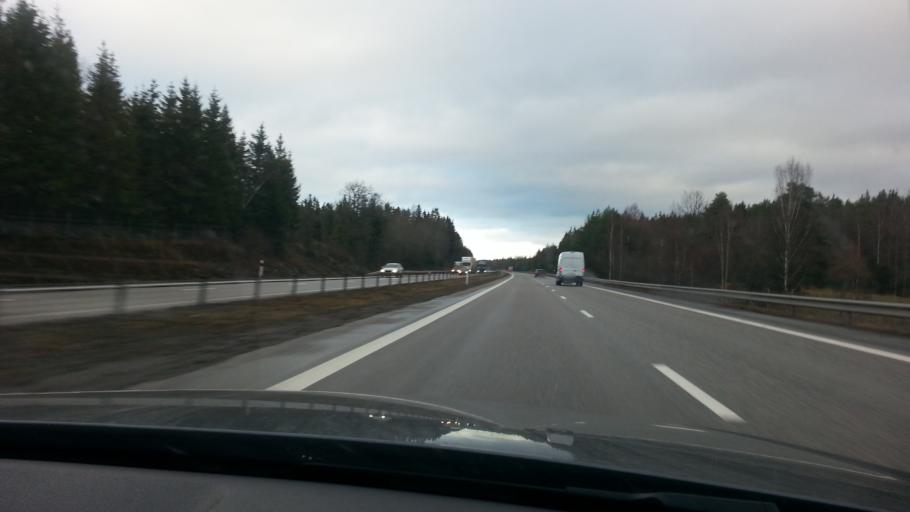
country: SE
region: Joenkoeping
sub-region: Jonkopings Kommun
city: Asa
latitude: 58.0993
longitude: 14.5544
